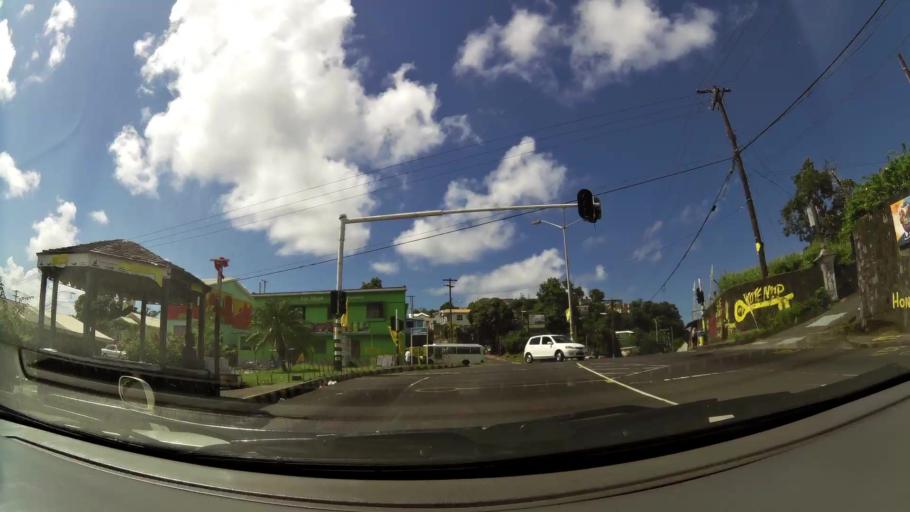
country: VC
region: Saint George
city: Kingstown
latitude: 13.1504
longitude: -61.2172
